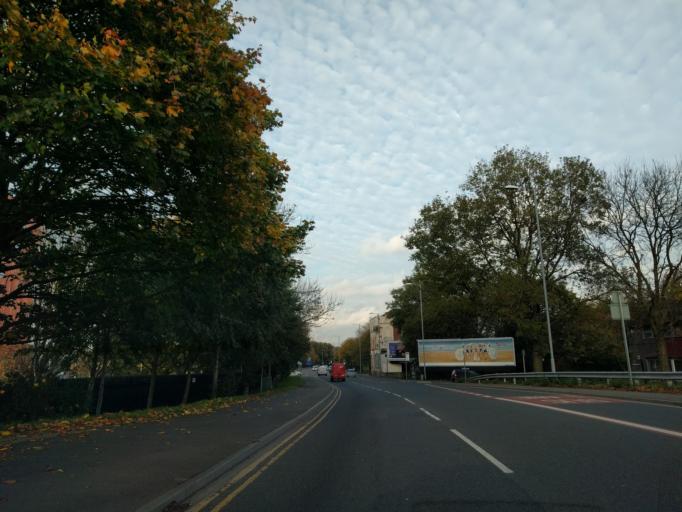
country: GB
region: England
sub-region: Manchester
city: Cheetham Hill
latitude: 53.4924
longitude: -2.2259
